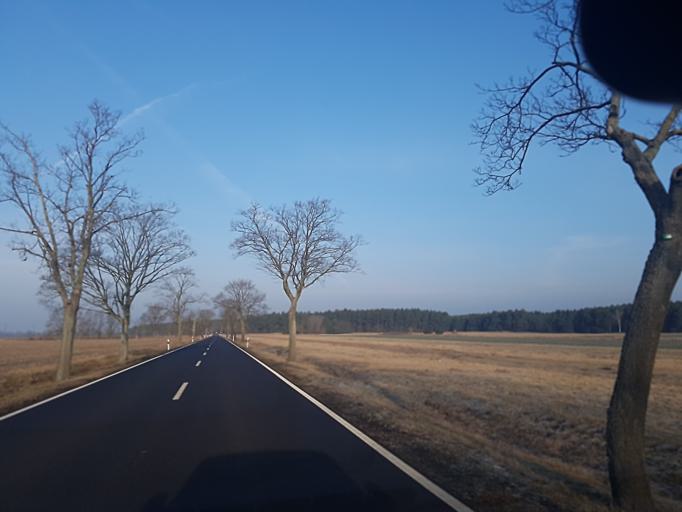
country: DE
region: Brandenburg
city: Golzow
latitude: 52.2667
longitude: 12.6500
